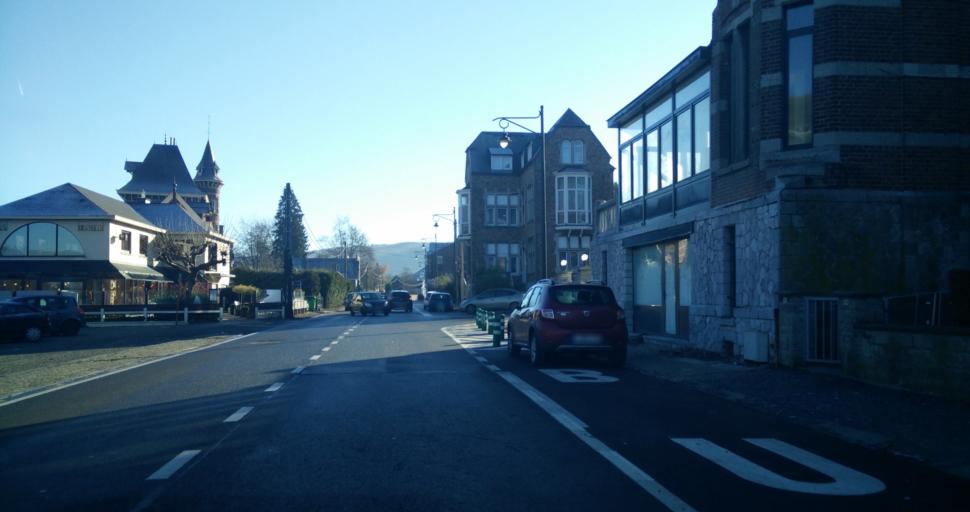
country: BE
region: Wallonia
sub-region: Province de Namur
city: Namur
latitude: 50.4238
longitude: 4.8734
